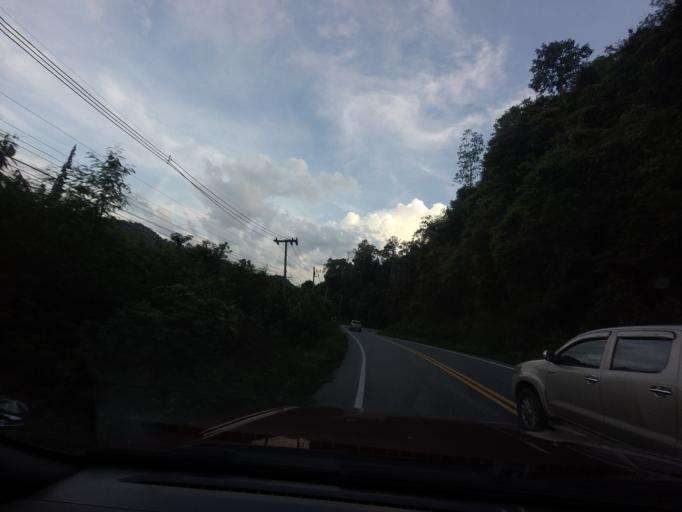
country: TH
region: Yala
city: Than To
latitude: 6.0418
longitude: 101.1978
